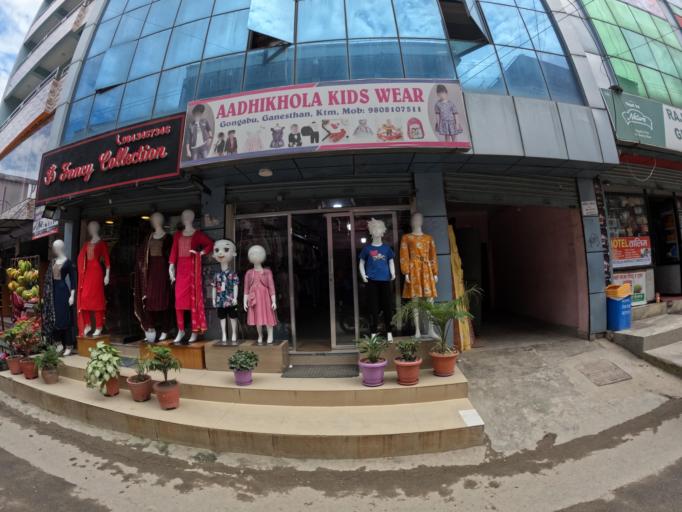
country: NP
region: Central Region
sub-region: Bagmati Zone
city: Kathmandu
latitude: 27.7402
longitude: 85.3141
